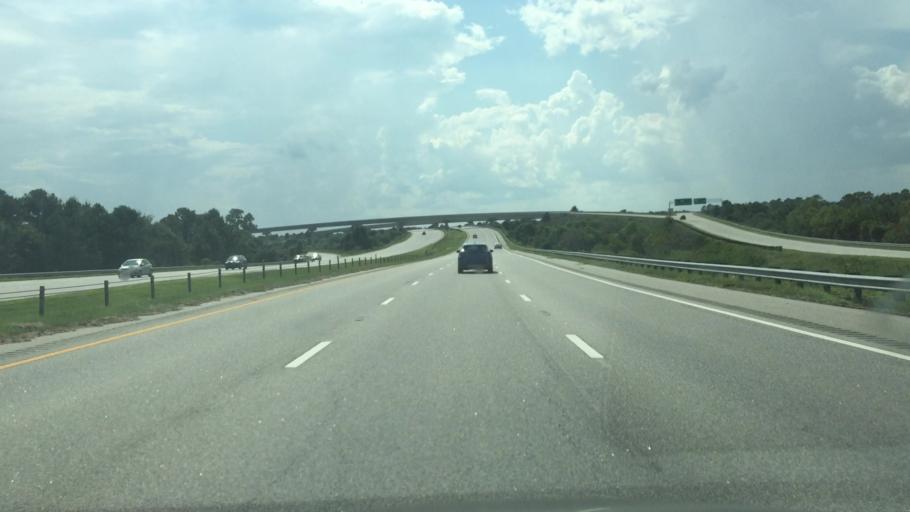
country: US
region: South Carolina
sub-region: Horry County
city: North Myrtle Beach
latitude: 33.8114
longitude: -78.7721
